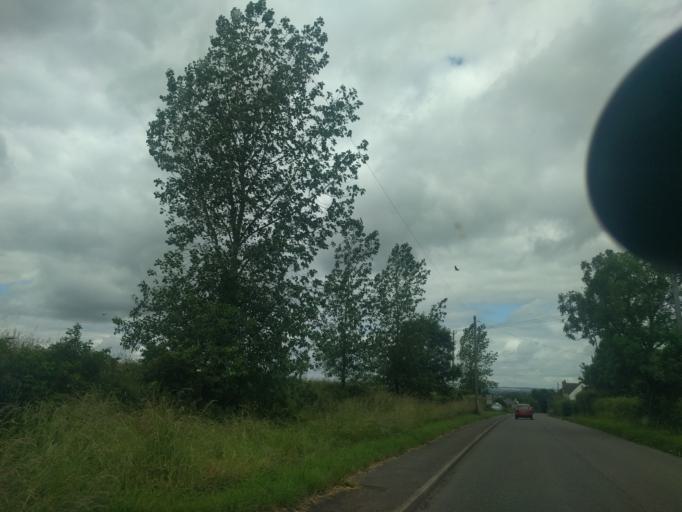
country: GB
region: England
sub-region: Wiltshire
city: Bratton
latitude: 51.3179
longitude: -2.1438
